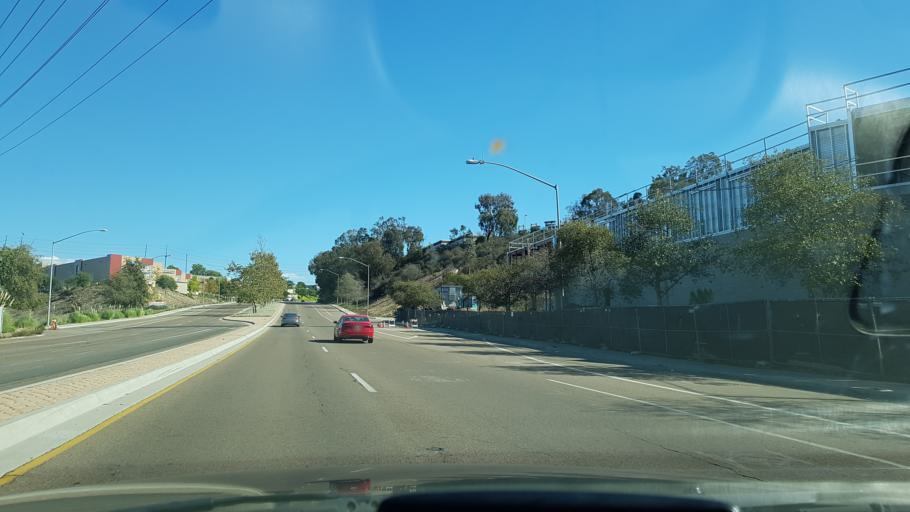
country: US
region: California
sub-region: San Diego County
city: Fairbanks Ranch
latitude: 32.8985
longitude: -117.1402
